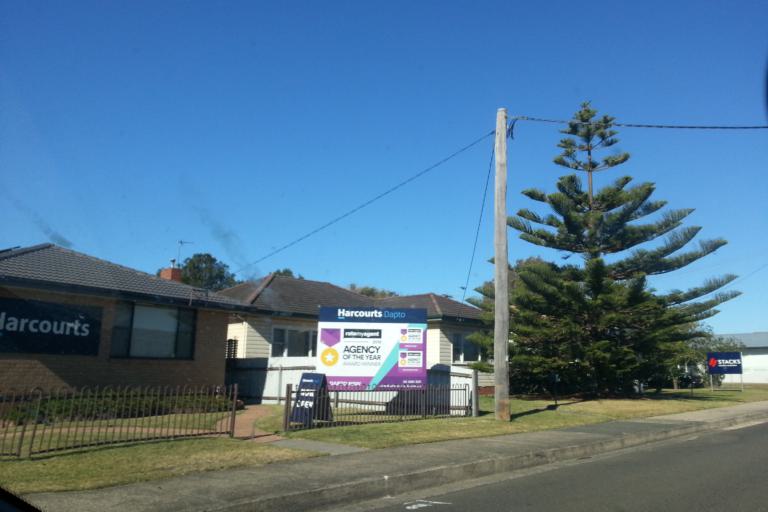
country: AU
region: New South Wales
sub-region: Wollongong
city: Dapto
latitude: -34.4913
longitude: 150.7964
